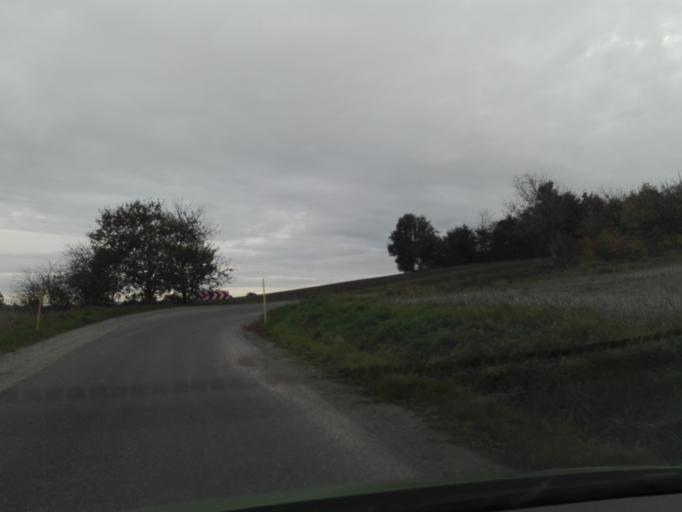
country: DK
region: Central Jutland
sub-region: Arhus Kommune
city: Marslet
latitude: 56.0592
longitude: 10.1670
